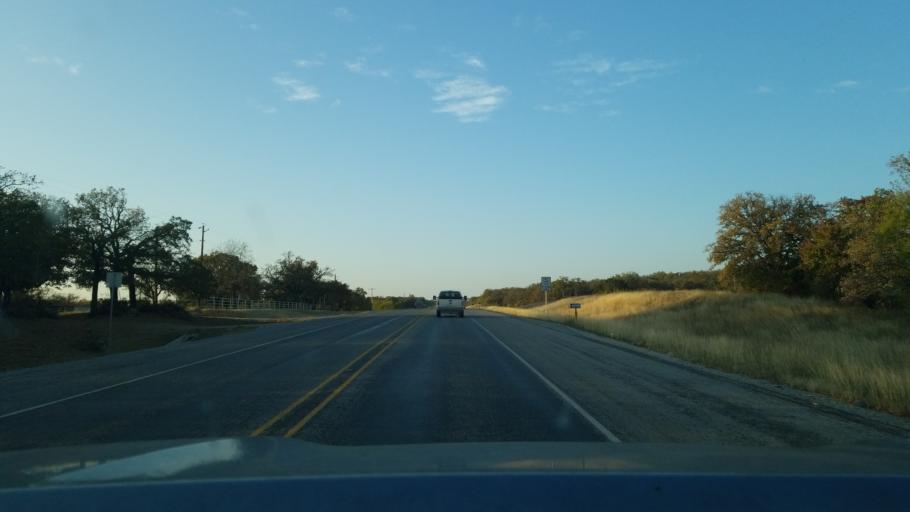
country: US
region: Texas
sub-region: Eastland County
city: Cisco
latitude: 32.3472
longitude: -98.9608
